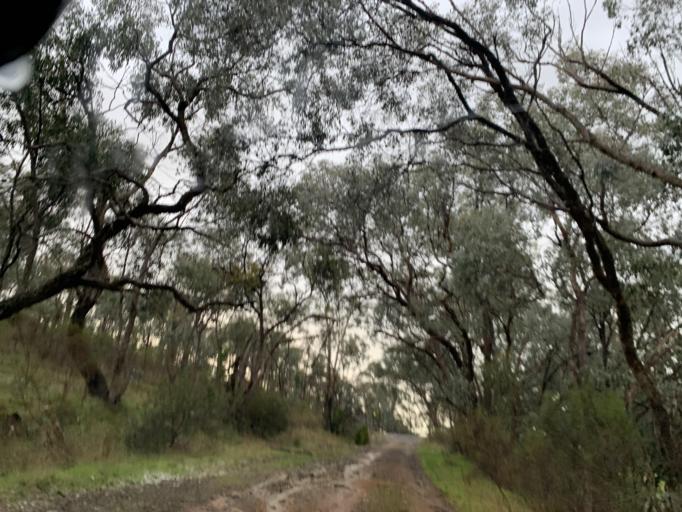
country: AU
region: Victoria
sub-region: Murrindindi
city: Kinglake West
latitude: -37.2187
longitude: 145.1340
